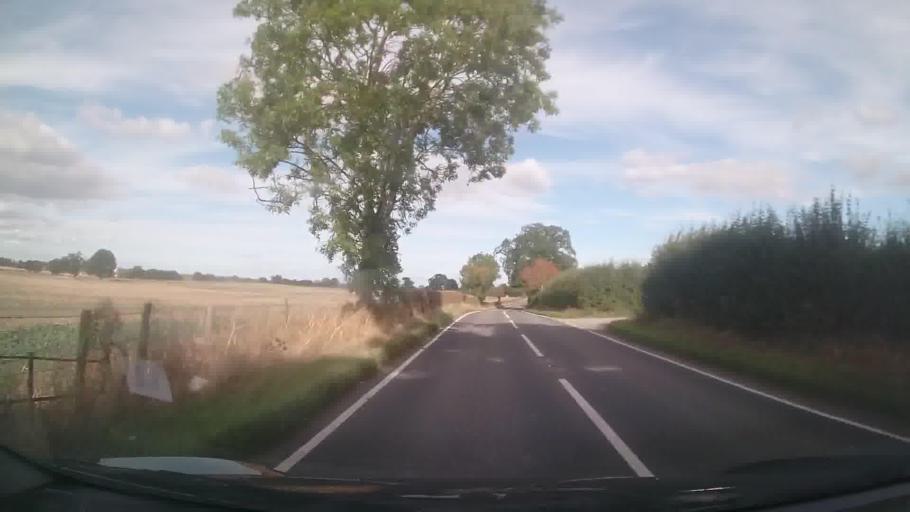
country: GB
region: England
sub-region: Shropshire
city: Great Hanwood
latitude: 52.6930
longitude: -2.7981
